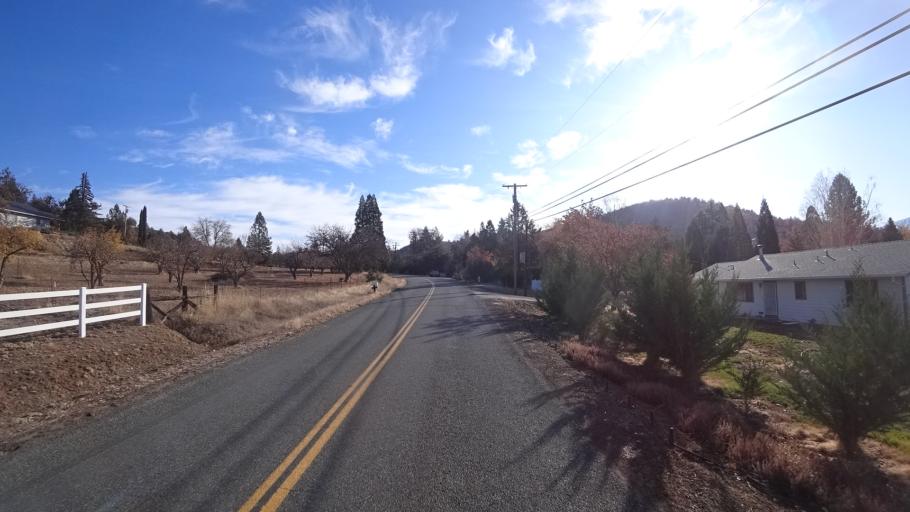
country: US
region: California
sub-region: Siskiyou County
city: Yreka
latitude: 41.6997
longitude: -122.6357
